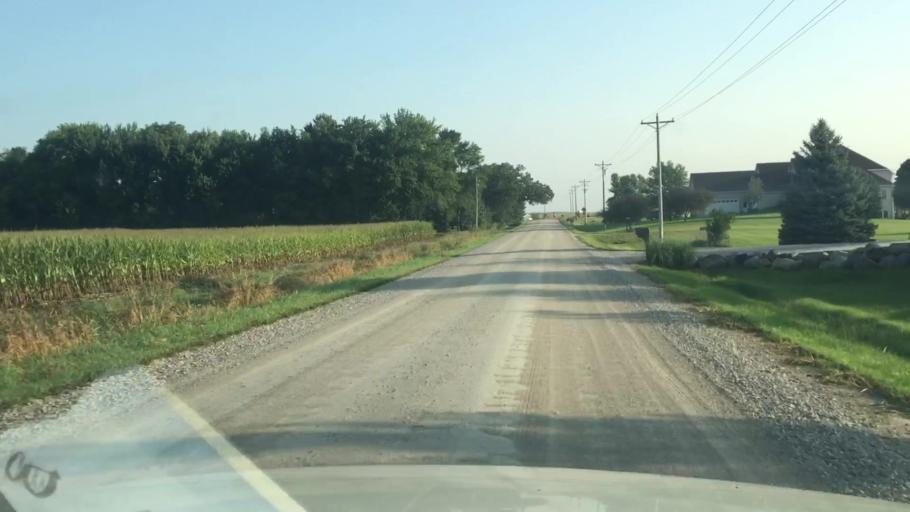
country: US
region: Iowa
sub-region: Story County
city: Huxley
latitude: 41.9148
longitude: -93.5765
